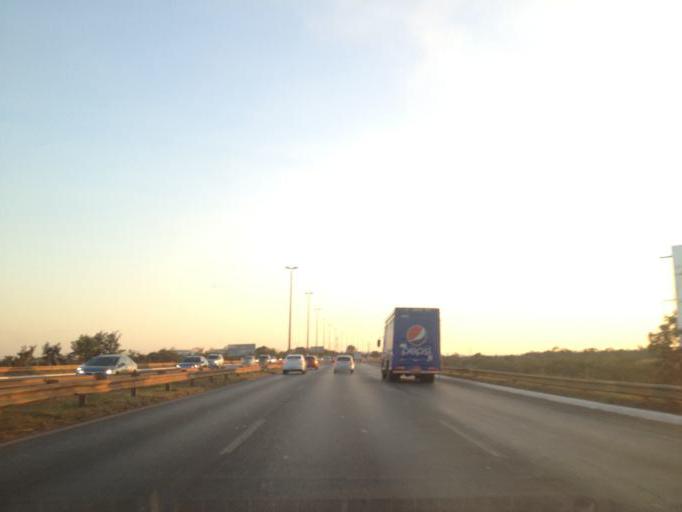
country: BR
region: Federal District
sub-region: Brasilia
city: Brasilia
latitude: -15.7904
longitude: -47.9514
